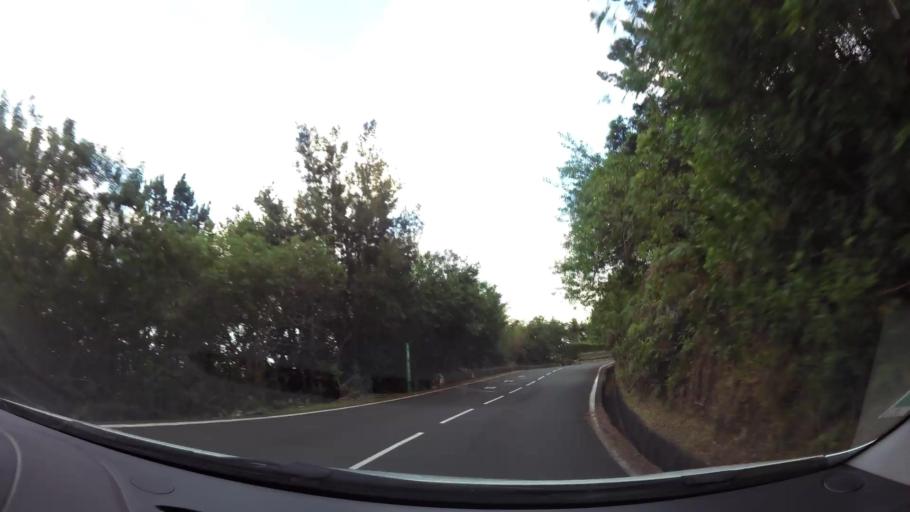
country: RE
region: Reunion
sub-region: Reunion
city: Saint-Denis
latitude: -20.9097
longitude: 55.4429
